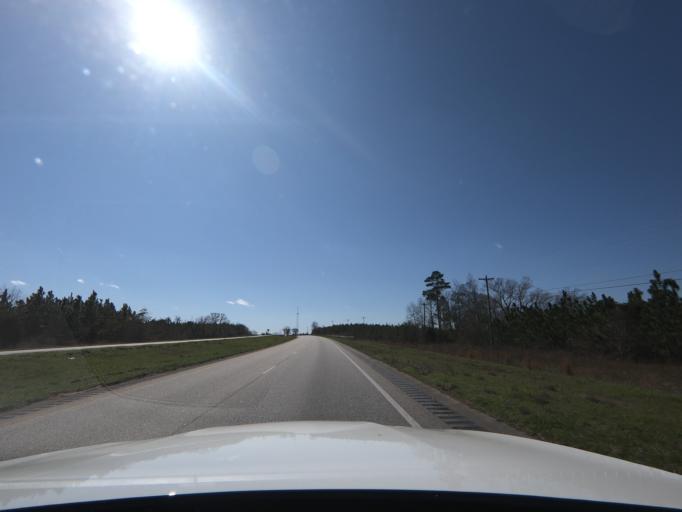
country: US
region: Alabama
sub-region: Henry County
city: Abbeville
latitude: 31.7192
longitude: -85.2691
